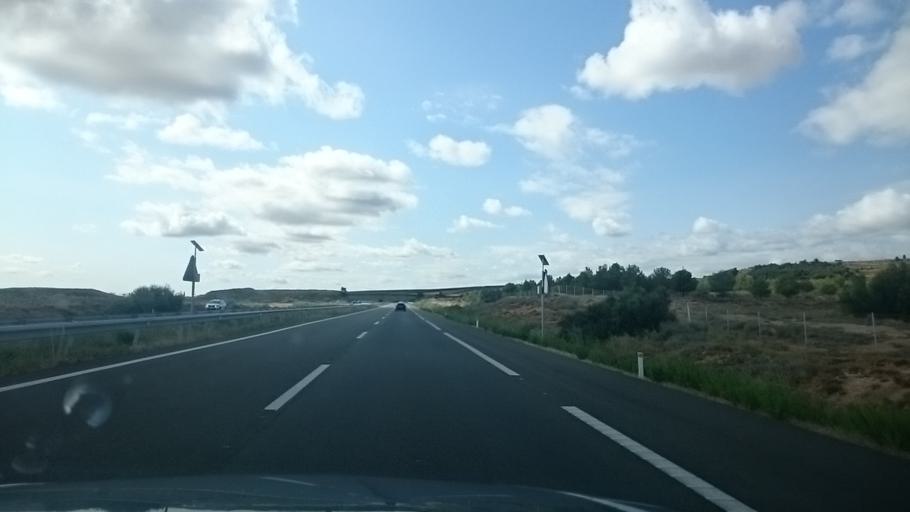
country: ES
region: Navarre
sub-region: Provincia de Navarra
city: Azagra
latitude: 42.2648
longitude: -1.9273
